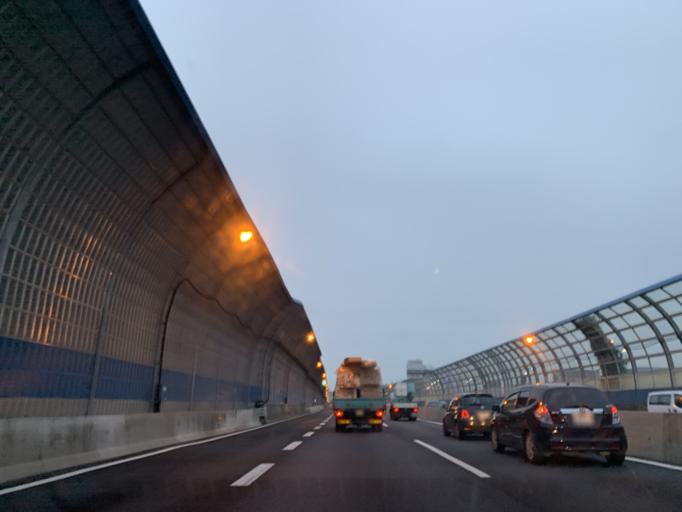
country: JP
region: Chiba
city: Funabashi
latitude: 35.6892
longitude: 139.9948
